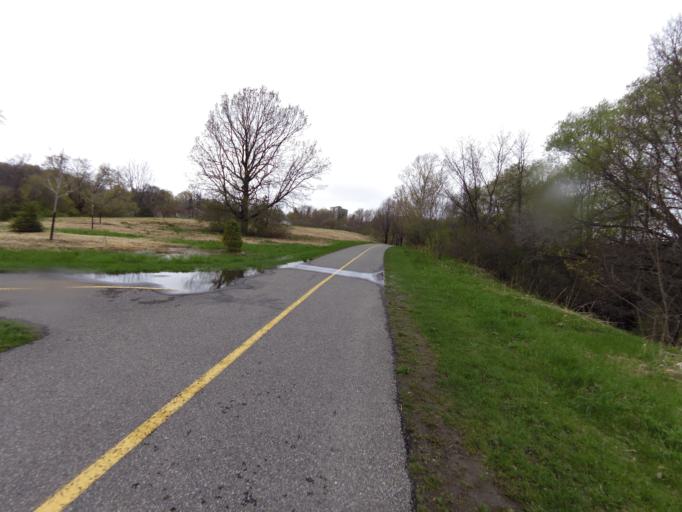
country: CA
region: Ontario
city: Bells Corners
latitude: 45.3602
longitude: -75.7815
